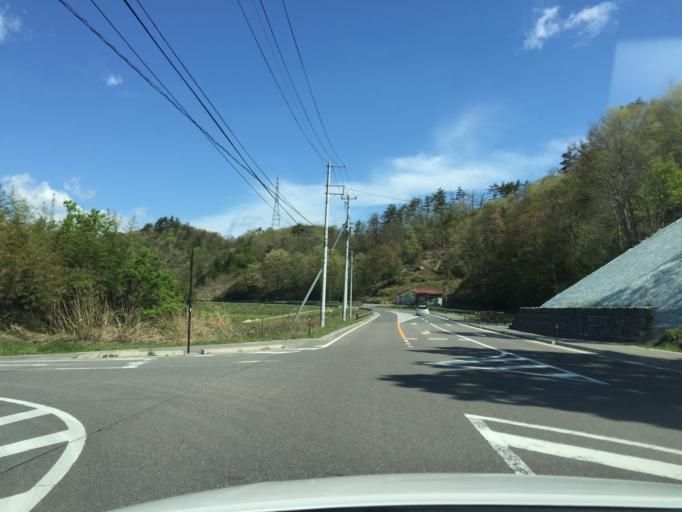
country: JP
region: Fukushima
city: Funehikimachi-funehiki
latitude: 37.5416
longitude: 140.5358
